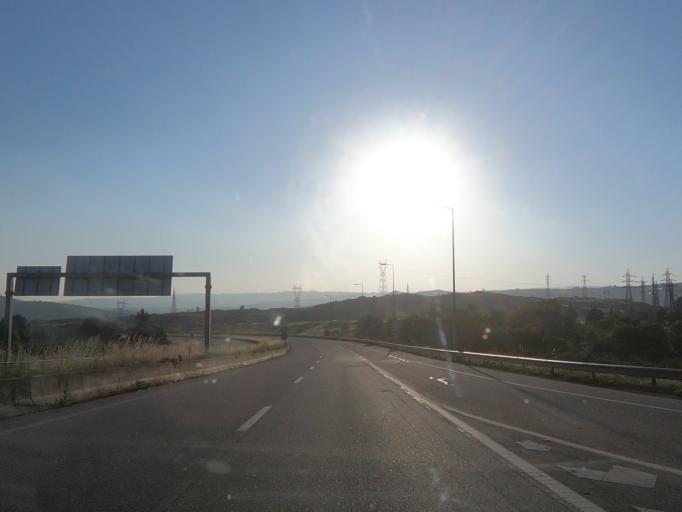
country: PT
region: Guarda
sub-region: Celorico da Beira
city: Celorico da Beira
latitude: 40.6302
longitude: -7.4151
